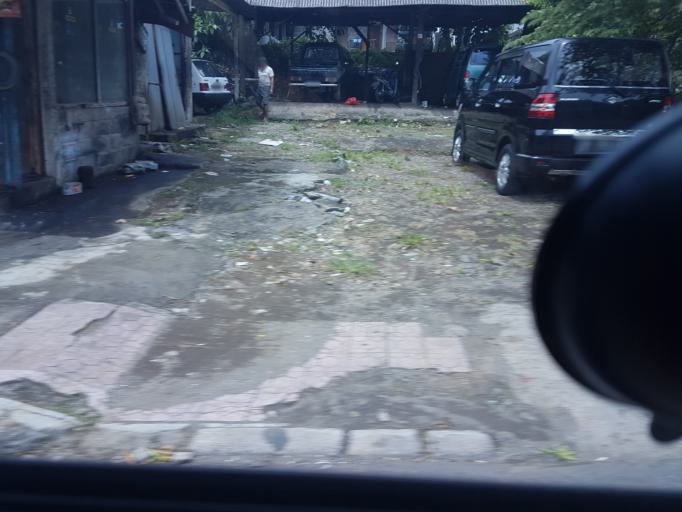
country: ID
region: Bali
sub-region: Kabupaten Gianyar
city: Ubud
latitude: -8.5231
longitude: 115.2926
